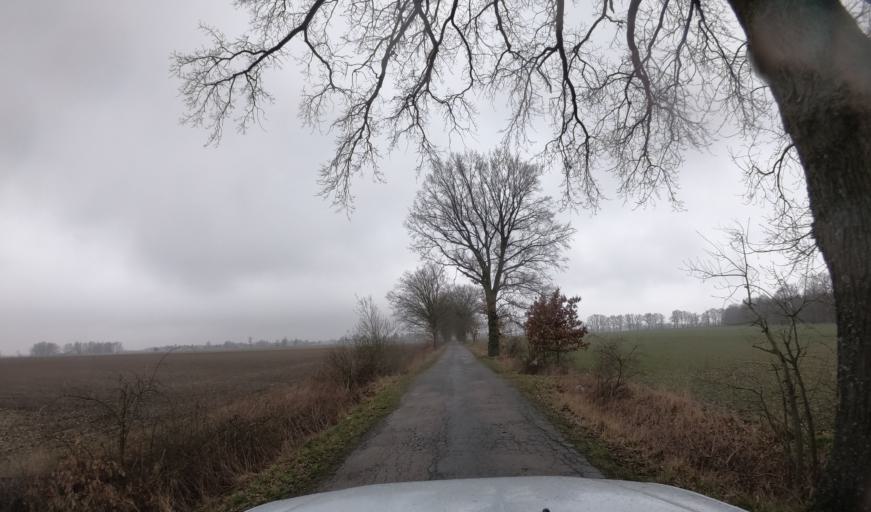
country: PL
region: West Pomeranian Voivodeship
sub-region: Powiat kamienski
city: Kamien Pomorski
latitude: 53.9067
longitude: 14.8153
